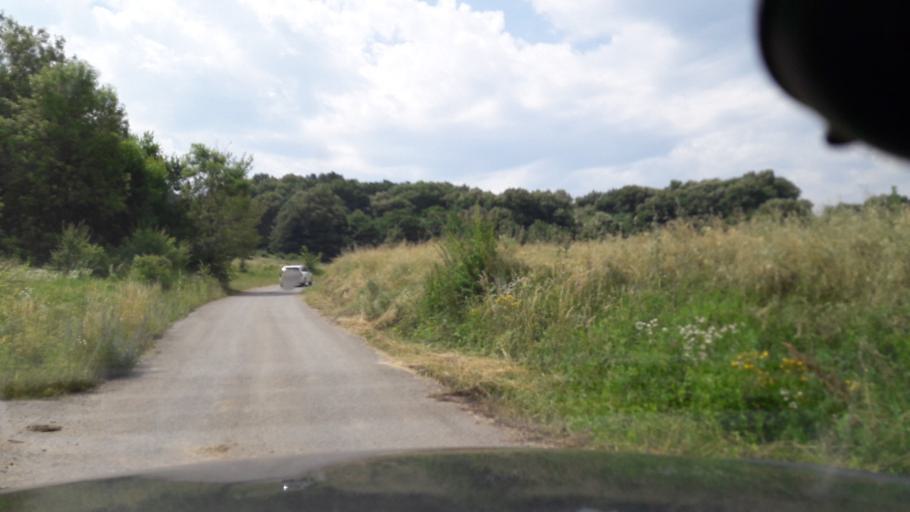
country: RS
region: Central Serbia
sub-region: Belgrade
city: Sopot
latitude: 44.6185
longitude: 20.6026
